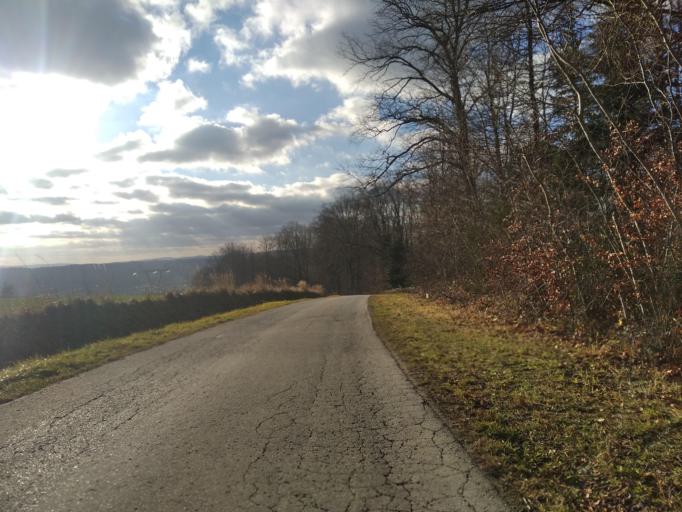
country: PL
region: Subcarpathian Voivodeship
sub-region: Powiat strzyzowski
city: Babica
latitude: 49.9460
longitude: 21.8725
